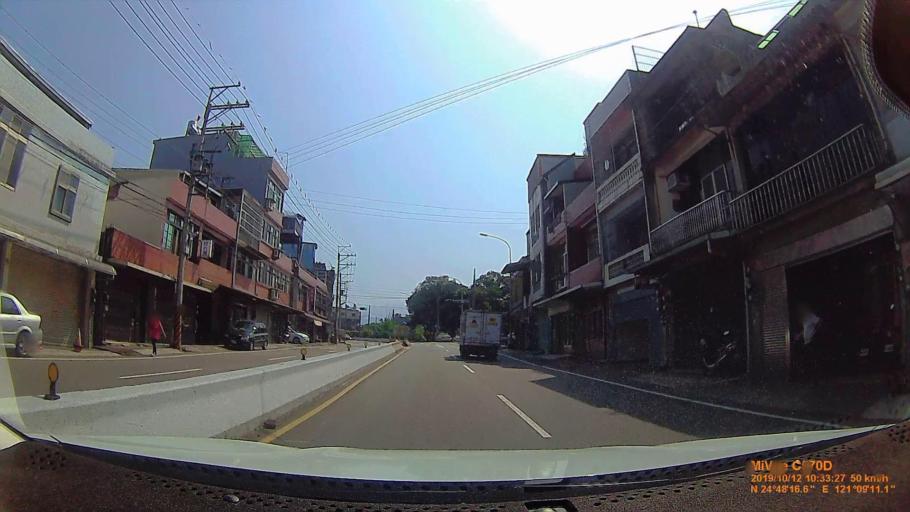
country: TW
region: Taiwan
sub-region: Hsinchu
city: Zhubei
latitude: 24.8046
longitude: 121.1531
